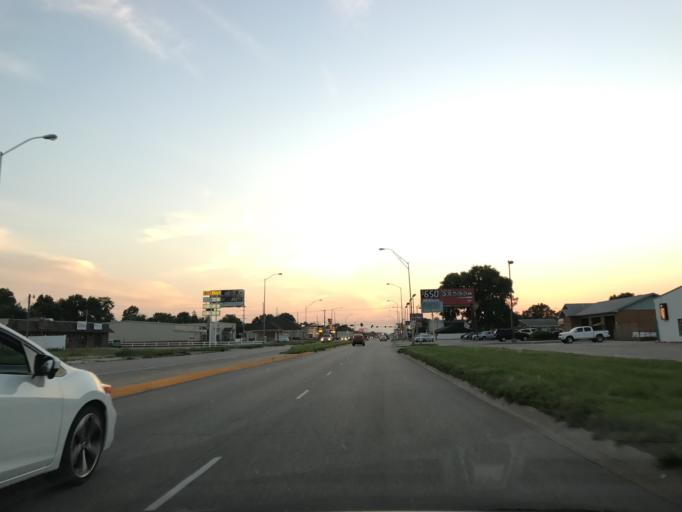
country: US
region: Nebraska
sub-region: Platte County
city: Columbus
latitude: 41.4385
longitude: -97.3461
